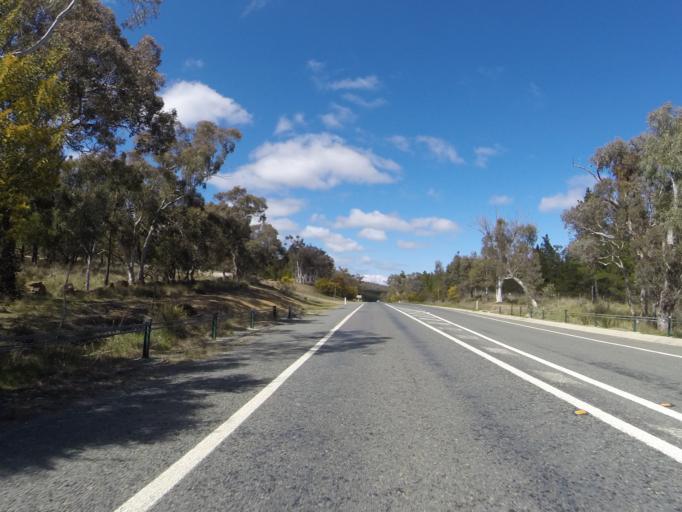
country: AU
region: New South Wales
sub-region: Queanbeyan
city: Queanbeyan
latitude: -35.2610
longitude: 149.2630
